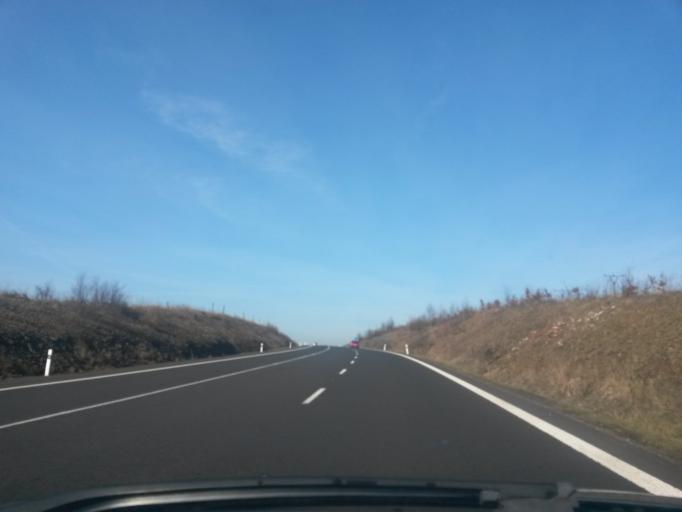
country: CZ
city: Krasna Lipa
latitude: 50.4836
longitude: 13.3137
